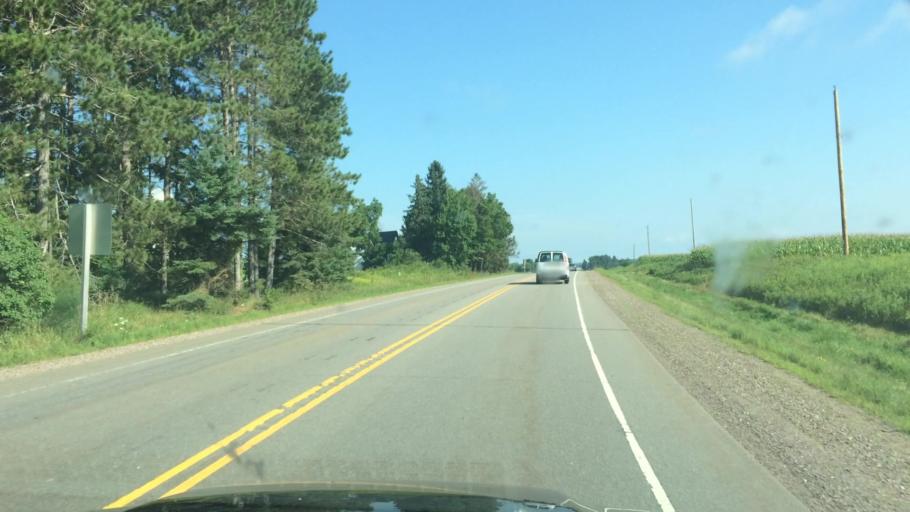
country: US
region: Wisconsin
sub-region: Lincoln County
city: Merrill
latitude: 45.1515
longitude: -89.4668
